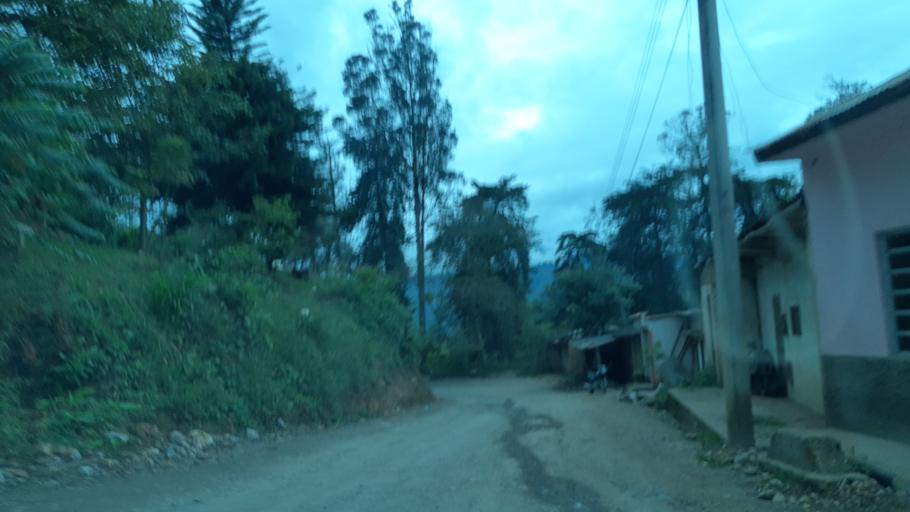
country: CO
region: Boyaca
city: Garagoa
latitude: 5.0856
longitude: -73.3560
